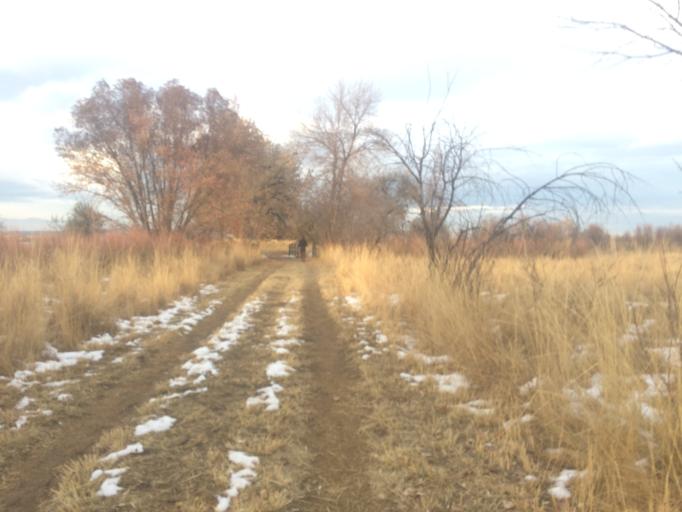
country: US
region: Colorado
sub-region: Boulder County
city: Gunbarrel
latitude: 40.0227
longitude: -105.1546
